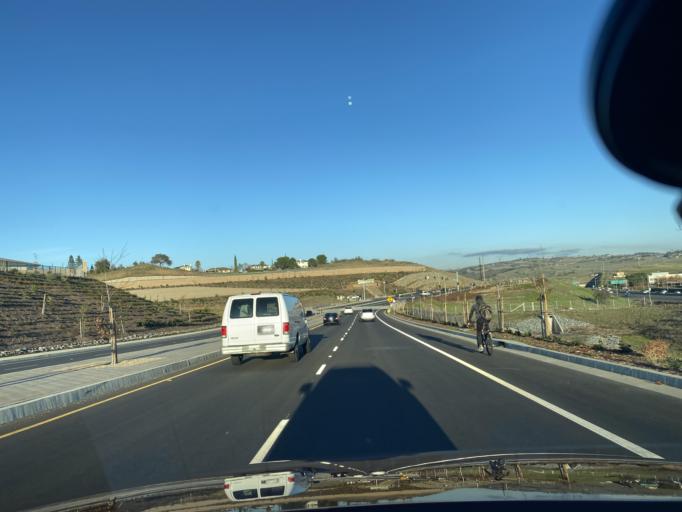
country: US
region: California
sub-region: El Dorado County
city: El Dorado Hills
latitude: 38.6497
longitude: -121.0826
